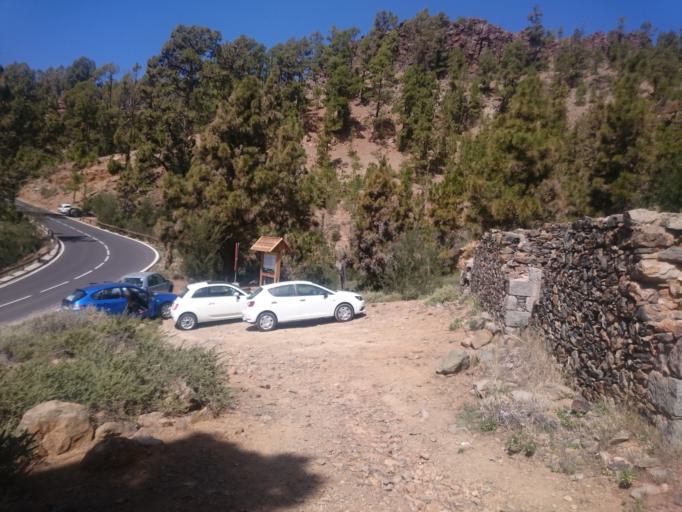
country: ES
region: Canary Islands
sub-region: Provincia de Santa Cruz de Tenerife
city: Vilaflor
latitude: 28.1889
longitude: -16.6568
